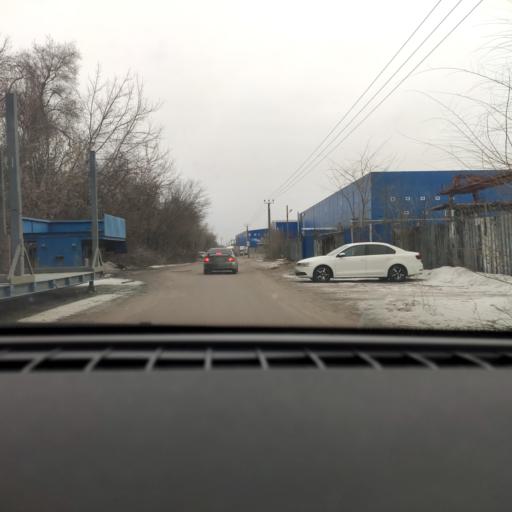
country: RU
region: Voronezj
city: Voronezh
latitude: 51.6505
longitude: 39.2652
